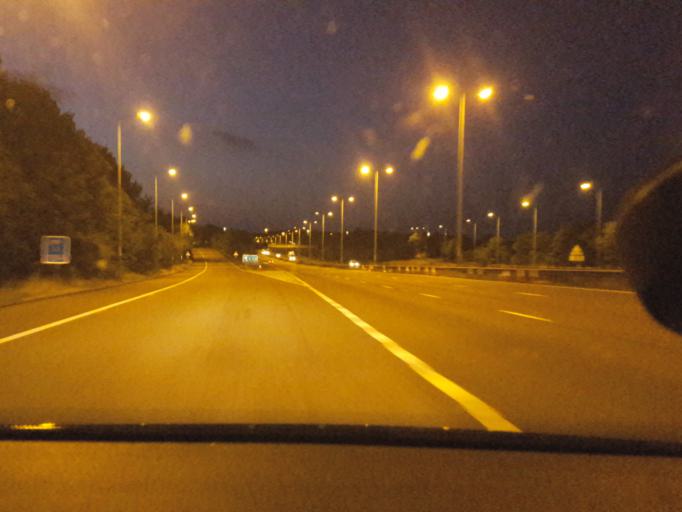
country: GB
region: England
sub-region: Leicestershire
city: Shepshed
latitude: 52.7561
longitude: -1.2742
